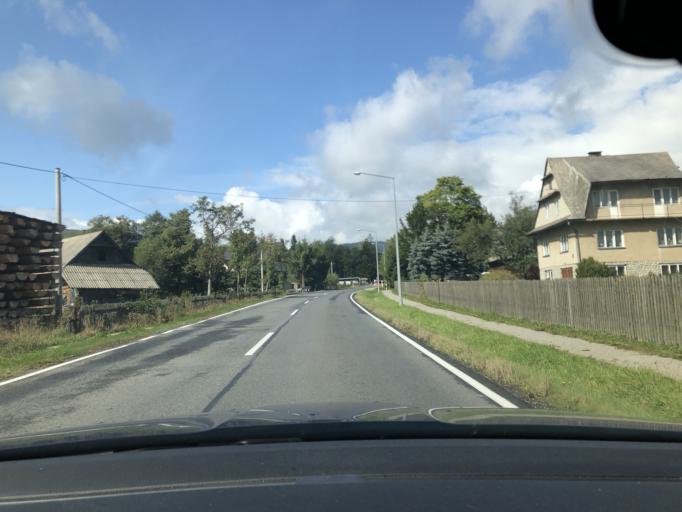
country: PL
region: Lesser Poland Voivodeship
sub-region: Powiat nowotarski
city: Zubrzyca Gorna
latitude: 49.5688
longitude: 19.6395
